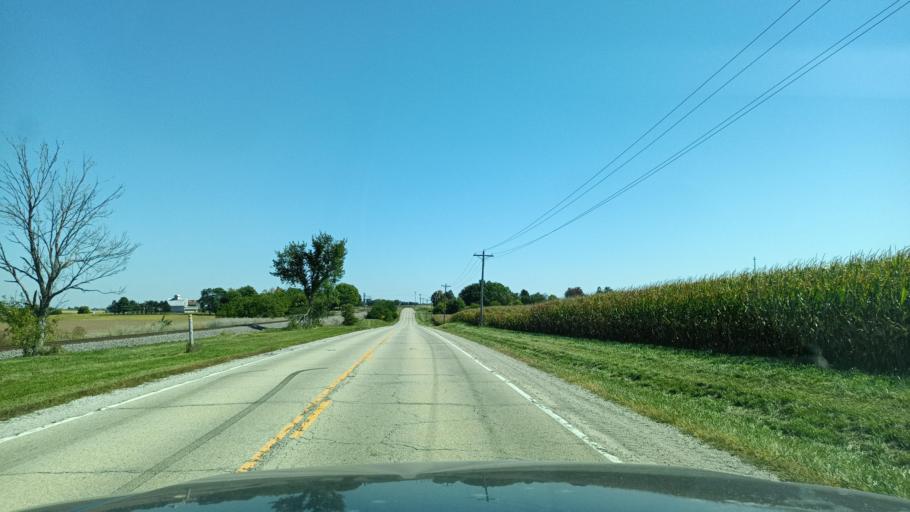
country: US
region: Illinois
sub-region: Woodford County
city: Eureka
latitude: 40.6268
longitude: -89.3053
